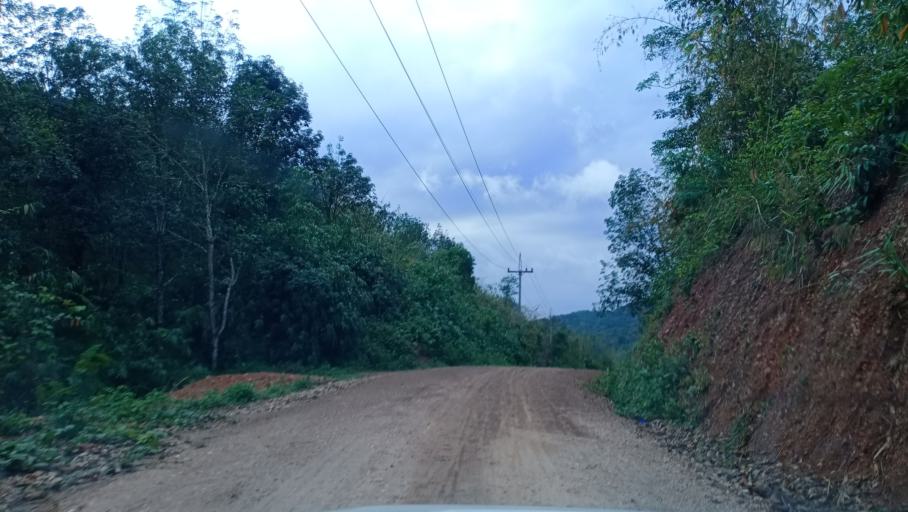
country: LA
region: Phongsali
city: Khoa
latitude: 21.1851
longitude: 102.7032
